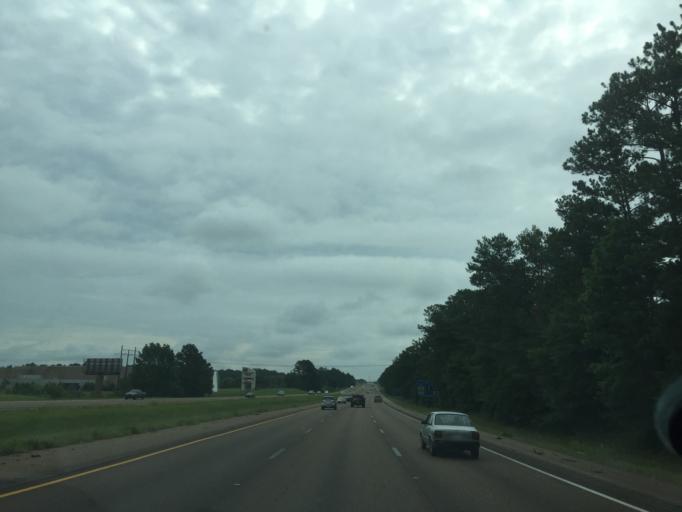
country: US
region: Mississippi
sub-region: Rankin County
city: Pearl
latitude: 32.2681
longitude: -90.0932
